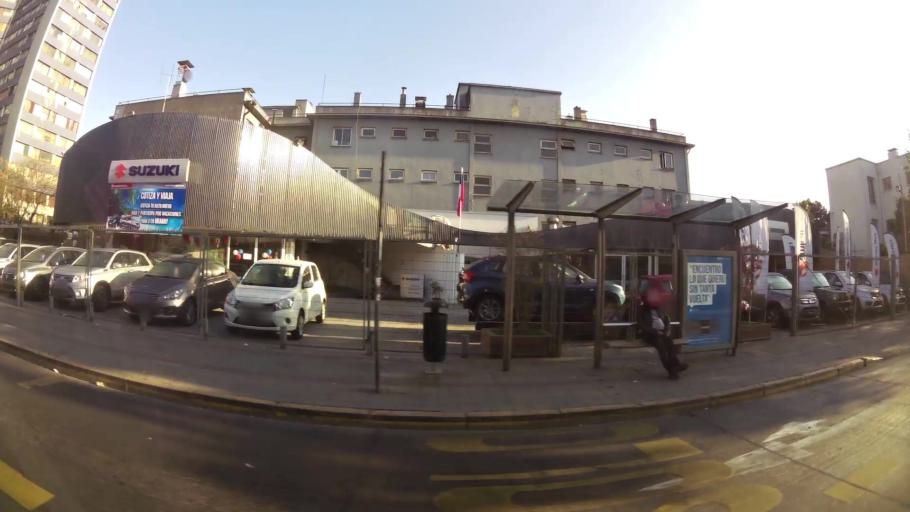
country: CL
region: Santiago Metropolitan
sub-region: Provincia de Santiago
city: Santiago
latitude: -33.4424
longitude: -70.6294
